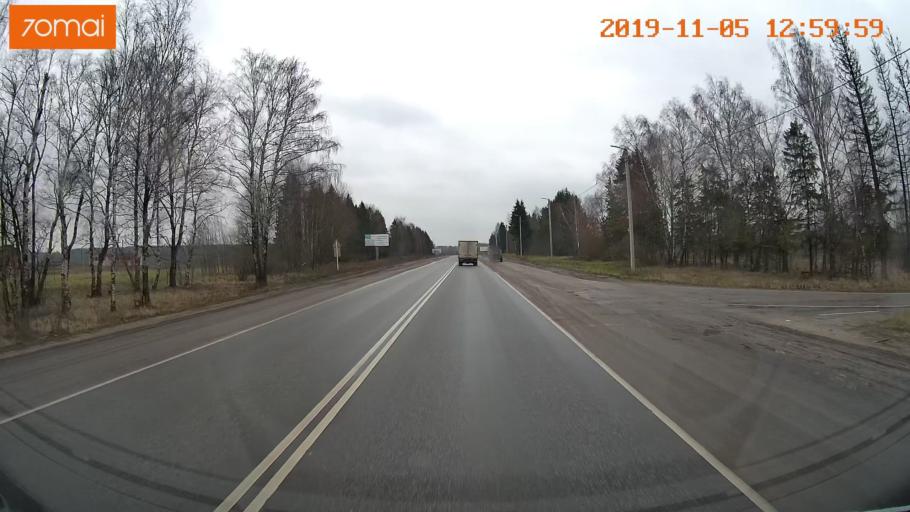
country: RU
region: Ivanovo
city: Kokhma
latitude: 56.9157
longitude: 41.1385
